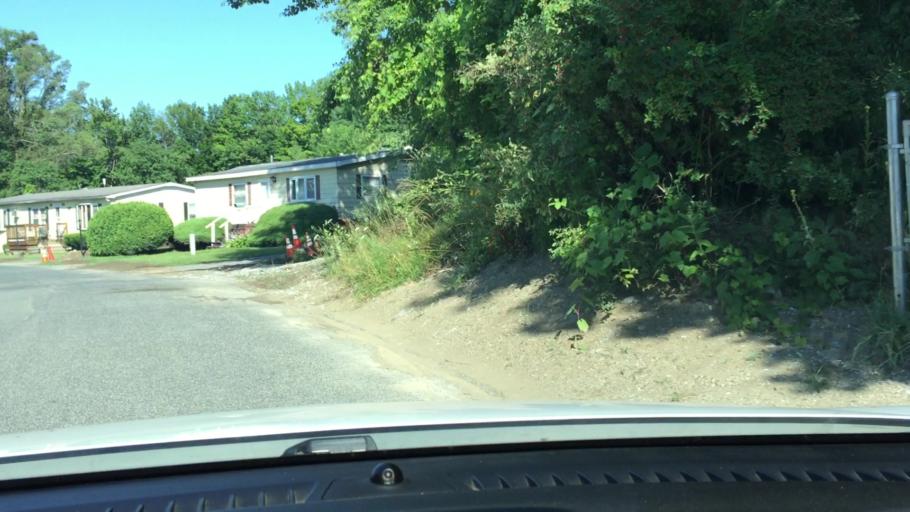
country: US
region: Massachusetts
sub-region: Berkshire County
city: Pittsfield
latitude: 42.4751
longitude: -73.2680
